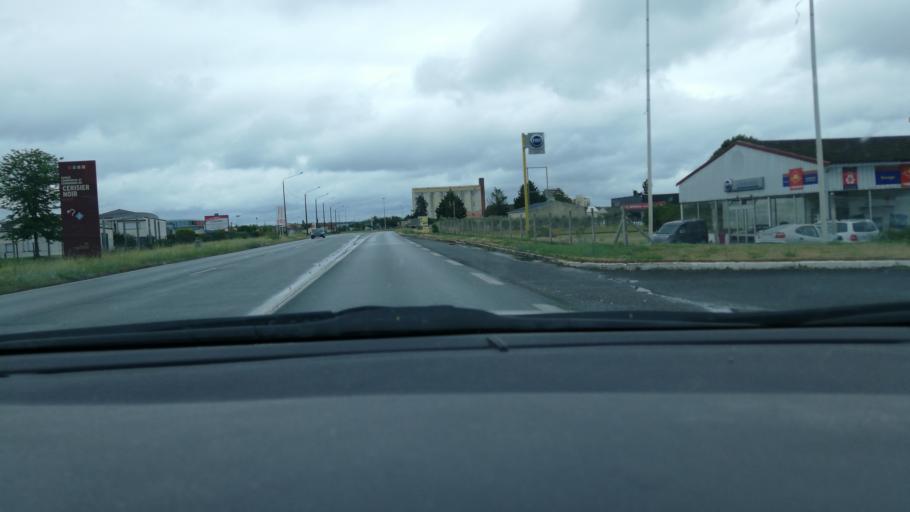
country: FR
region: Poitou-Charentes
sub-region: Departement de la Vienne
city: Naintre
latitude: 46.7543
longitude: 0.4843
